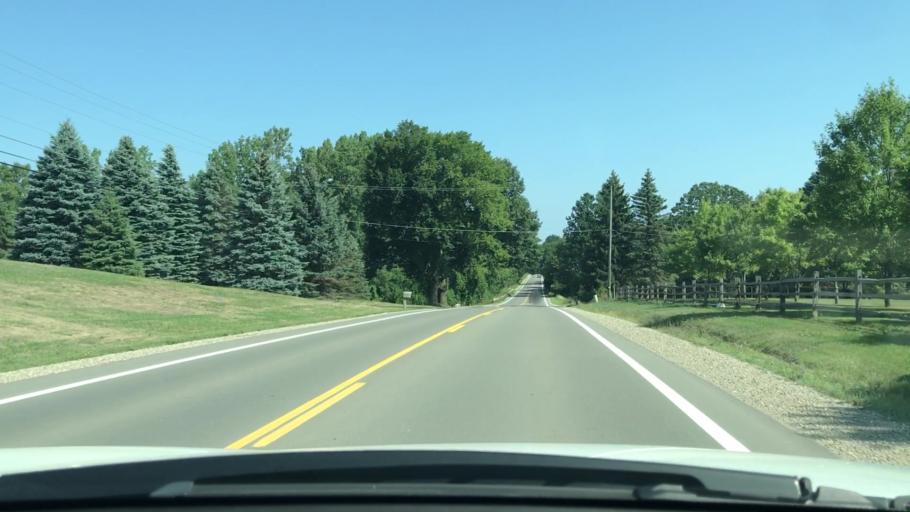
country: US
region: Michigan
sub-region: Oakland County
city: Oxford
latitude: 42.8000
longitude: -83.3332
